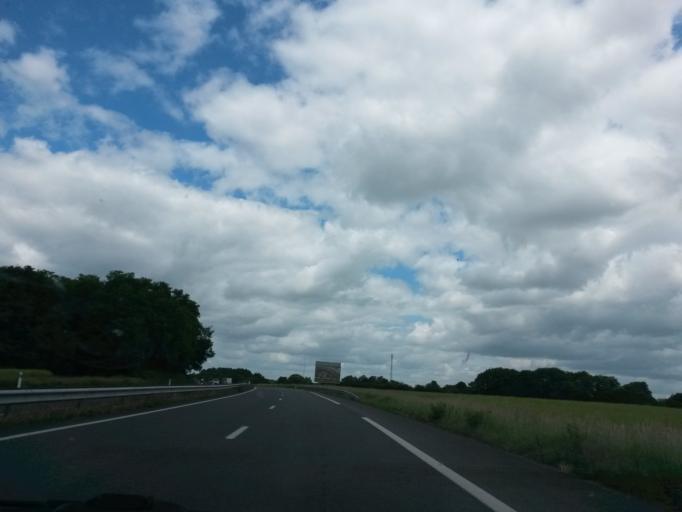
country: FR
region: Centre
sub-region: Departement du Cher
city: Herry
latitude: 47.2382
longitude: 3.0052
